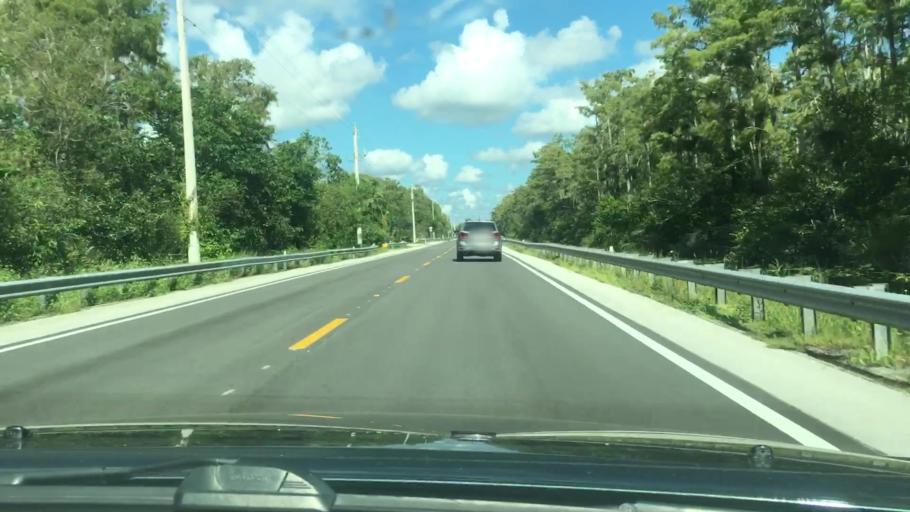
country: US
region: Florida
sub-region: Miami-Dade County
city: Kendall West
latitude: 25.8012
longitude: -80.8687
